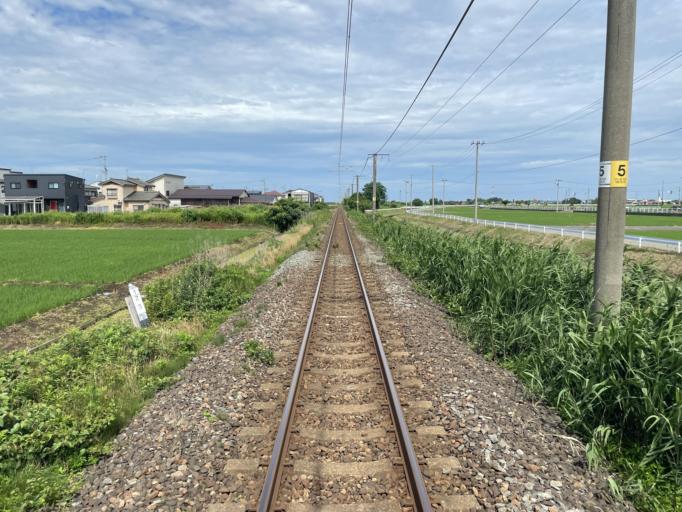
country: JP
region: Niigata
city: Shibata
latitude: 37.9429
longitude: 139.3005
